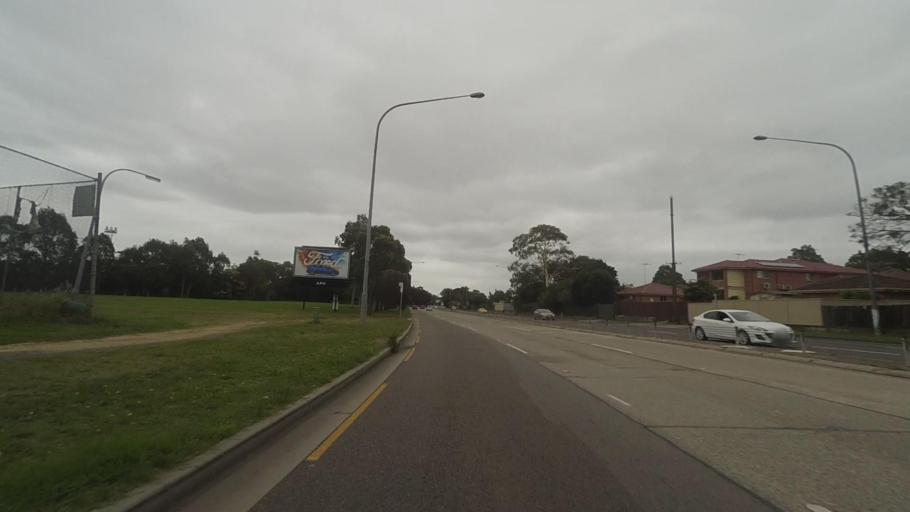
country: AU
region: New South Wales
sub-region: Auburn
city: Lidcombe
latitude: -33.8579
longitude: 151.0427
